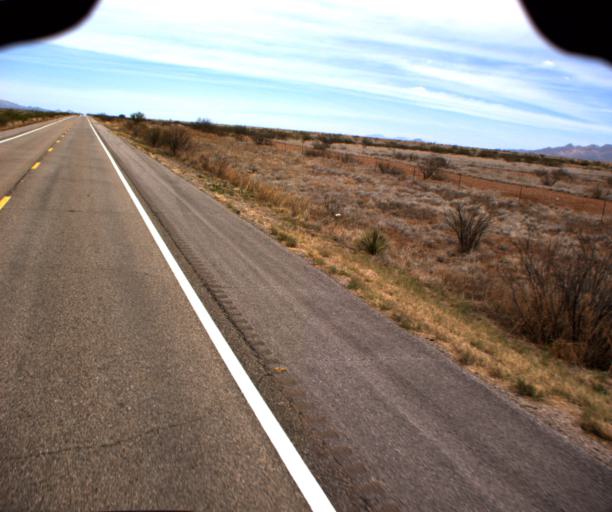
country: US
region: Arizona
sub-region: Cochise County
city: Pirtleville
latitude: 31.5062
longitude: -109.6382
